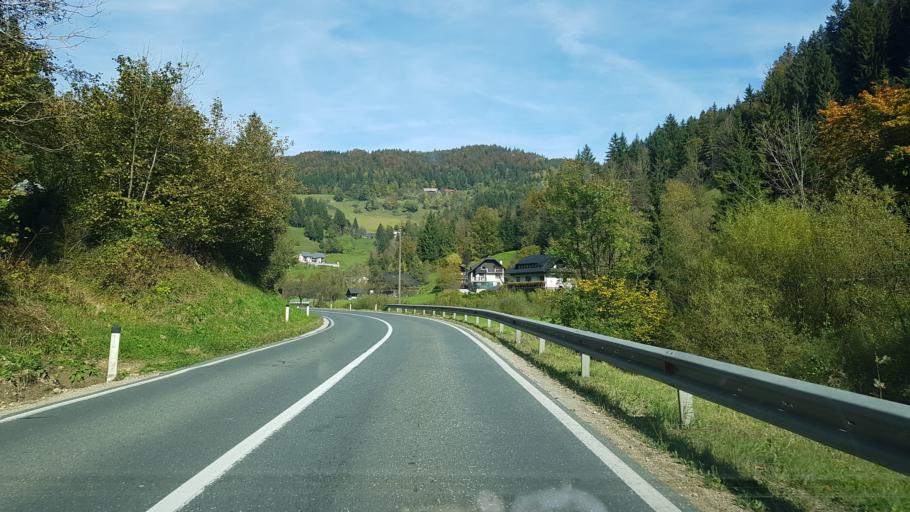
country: SI
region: Velenje
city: Velenje
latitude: 46.4053
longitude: 15.1789
